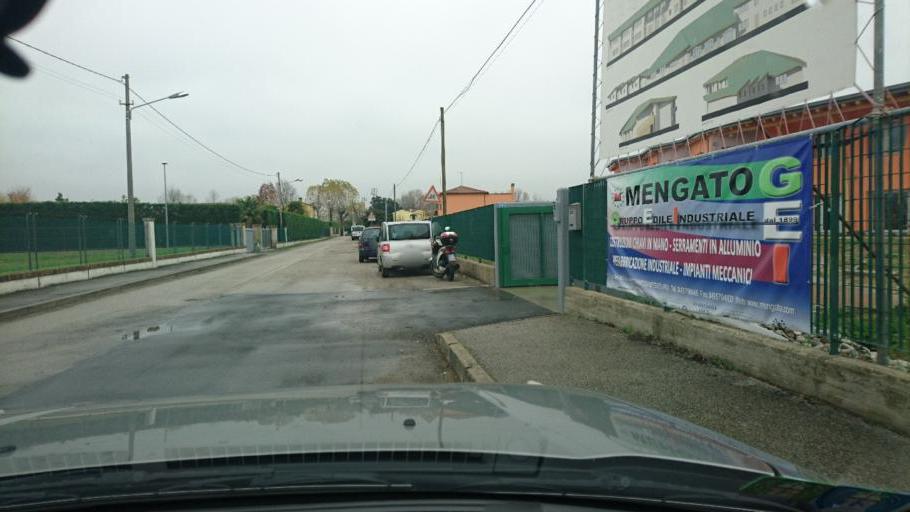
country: IT
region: Veneto
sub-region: Provincia di Padova
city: Padova
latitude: 45.4310
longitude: 11.8682
